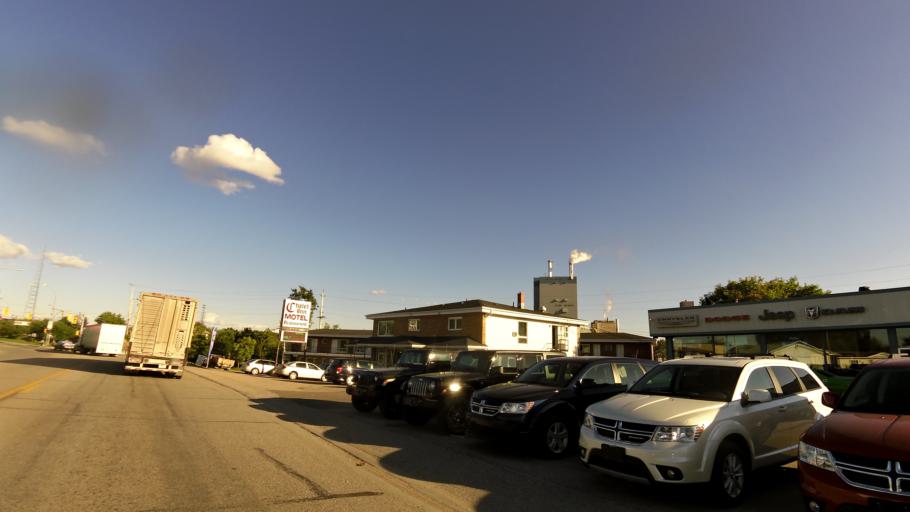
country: CA
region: Ontario
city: Dryden
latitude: 49.7872
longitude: -92.8462
